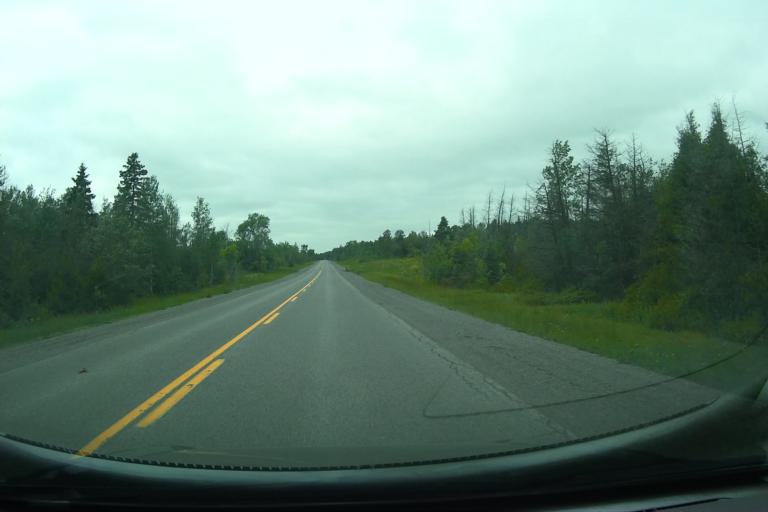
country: CA
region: Ontario
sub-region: Lanark County
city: Smiths Falls
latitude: 45.0115
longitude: -75.8350
